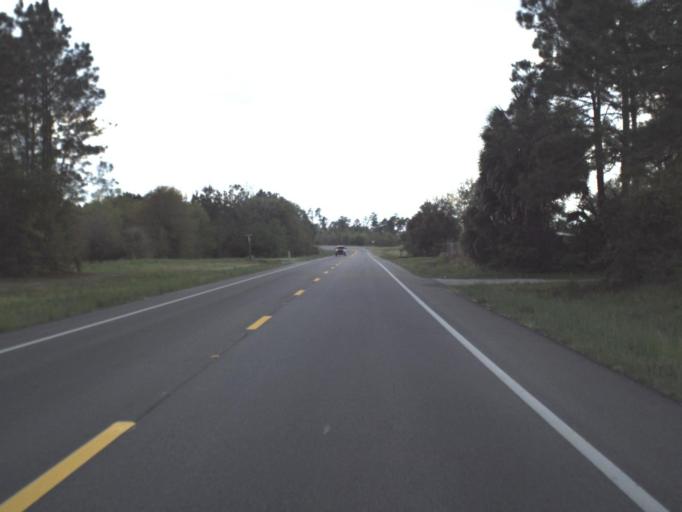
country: US
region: Florida
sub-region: Okaloosa County
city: Crestview
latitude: 30.8714
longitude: -86.5219
